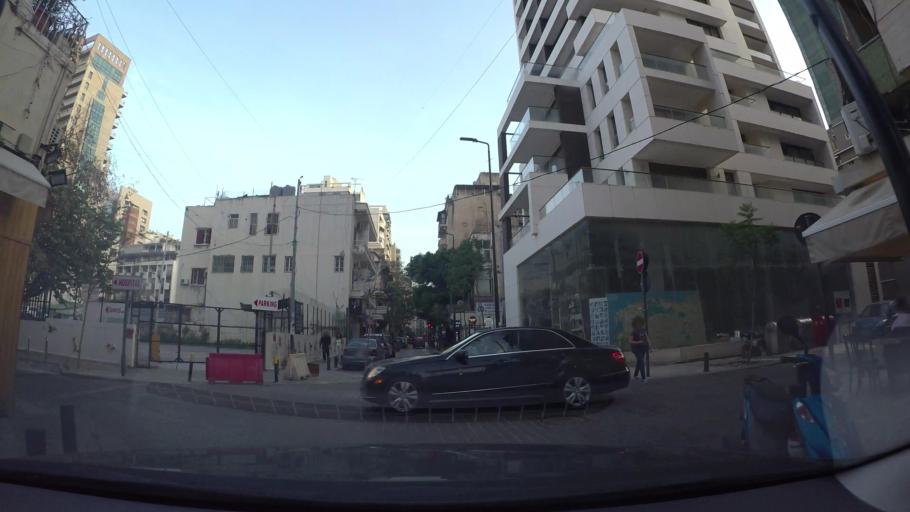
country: LB
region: Beyrouth
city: Ra's Bayrut
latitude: 33.8987
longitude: 35.4816
